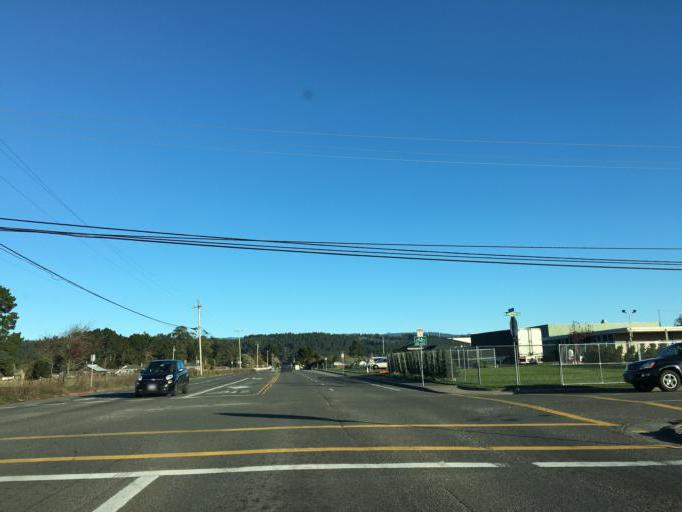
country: US
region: California
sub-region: Humboldt County
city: McKinleyville
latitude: 40.9562
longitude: -124.1107
